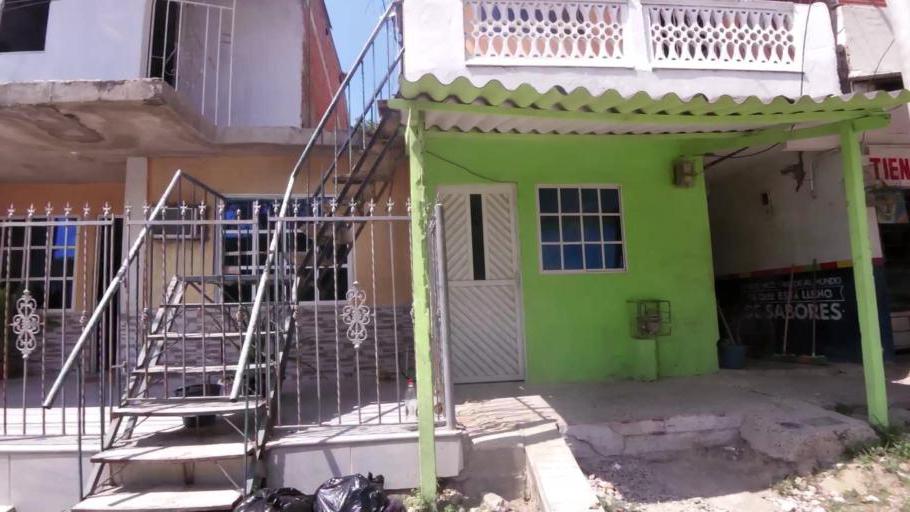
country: CO
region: Bolivar
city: Cartagena
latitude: 10.3553
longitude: -75.4989
